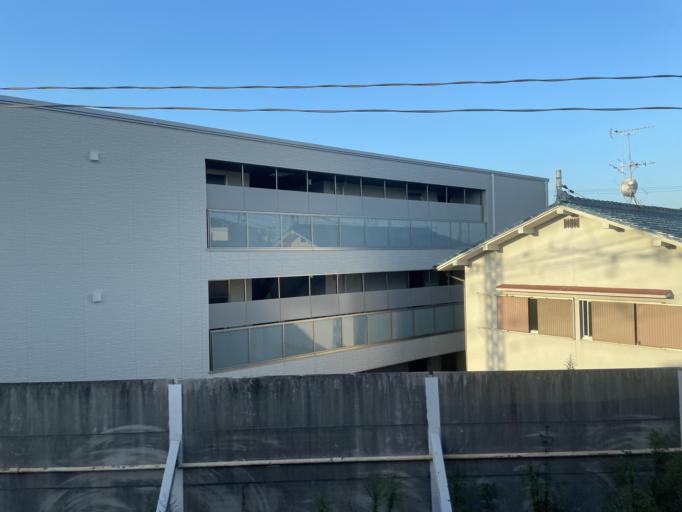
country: JP
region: Nara
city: Kashihara-shi
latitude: 34.5145
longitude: 135.7889
